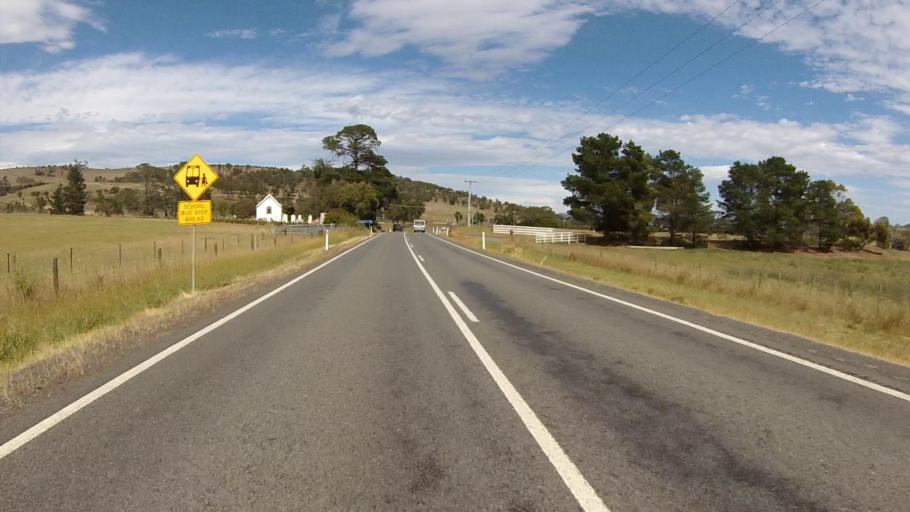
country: AU
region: Tasmania
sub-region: Brighton
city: Old Beach
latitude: -42.6906
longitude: 147.3460
